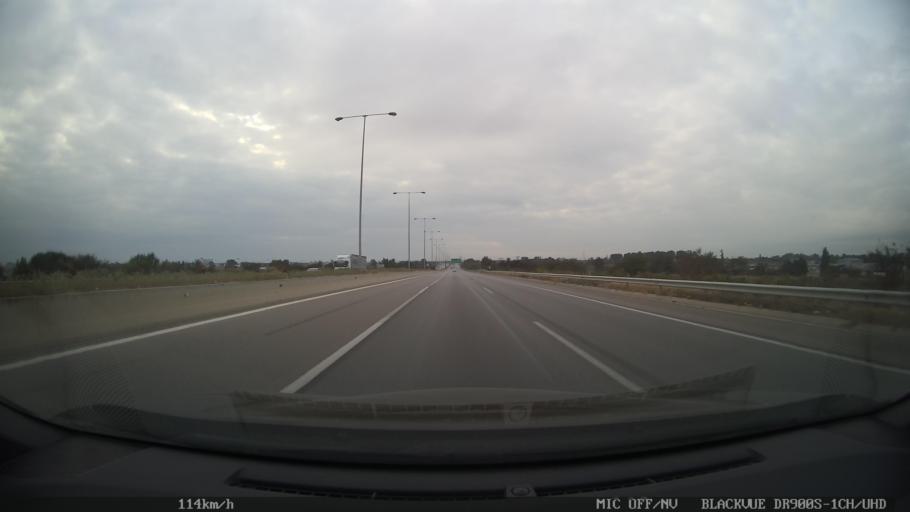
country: GR
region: Central Macedonia
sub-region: Nomos Thessalonikis
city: Nea Magnisia
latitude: 40.6653
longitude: 22.8364
